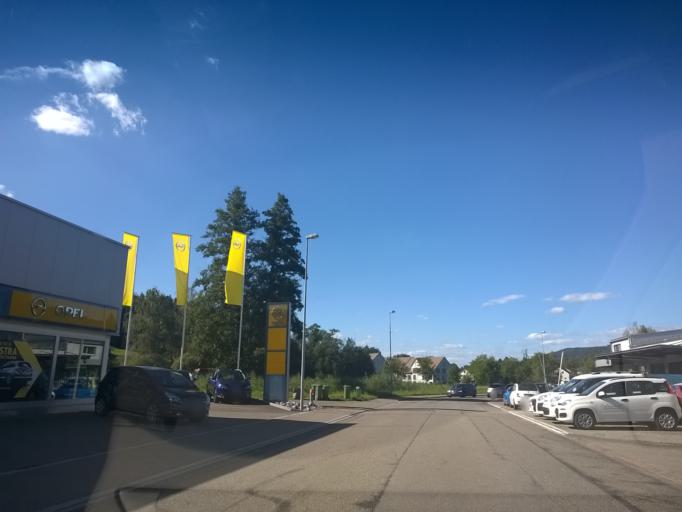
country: CH
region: Zurich
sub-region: Bezirk Buelach
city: Embrach / Kellersacker
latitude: 47.5102
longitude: 8.5893
